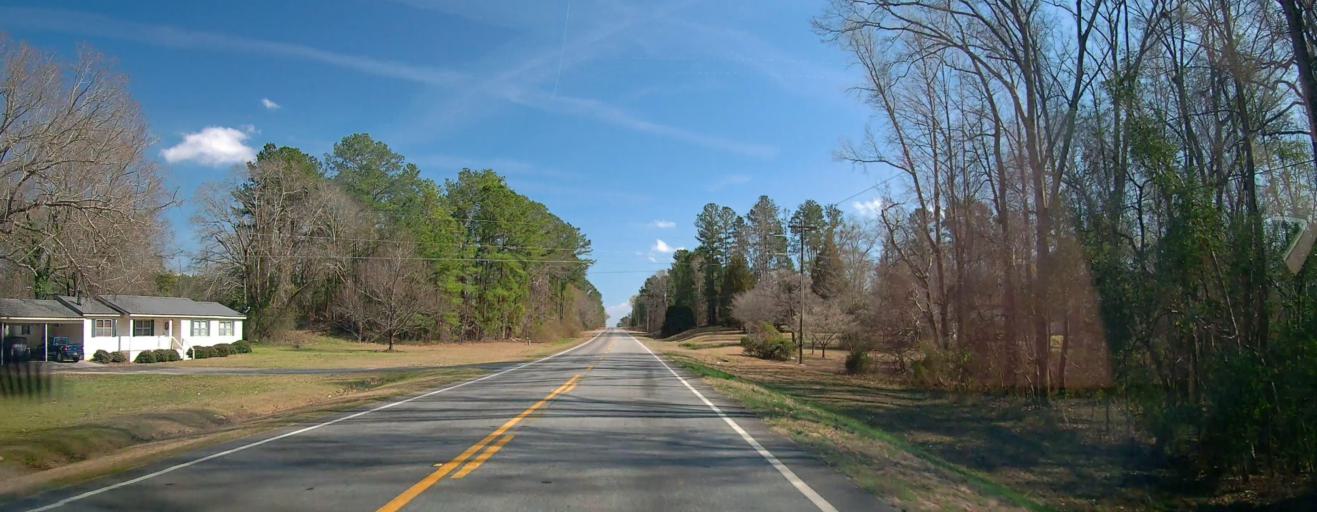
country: US
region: Georgia
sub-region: Wilkinson County
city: Gordon
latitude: 32.9012
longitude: -83.3709
